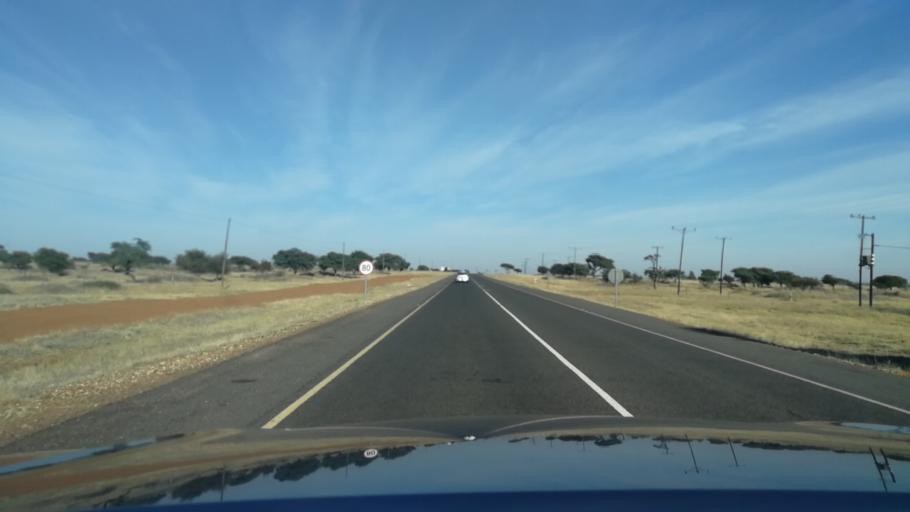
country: BW
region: South East
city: Janeng
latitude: -25.4702
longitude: 25.5348
